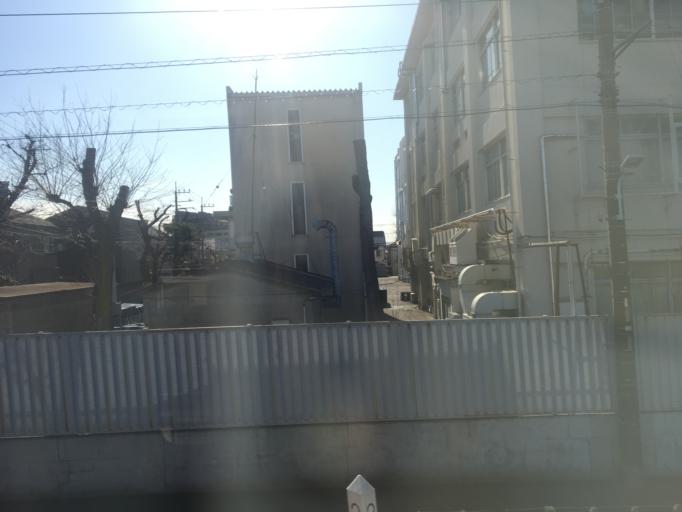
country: JP
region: Saitama
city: Kamifukuoka
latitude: 35.8667
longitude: 139.5179
